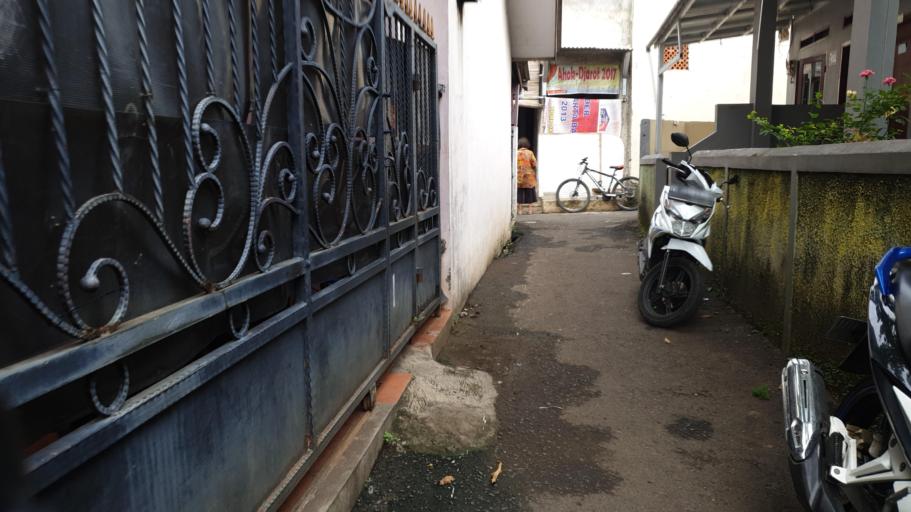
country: ID
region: West Java
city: Depok
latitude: -6.3341
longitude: 106.8229
